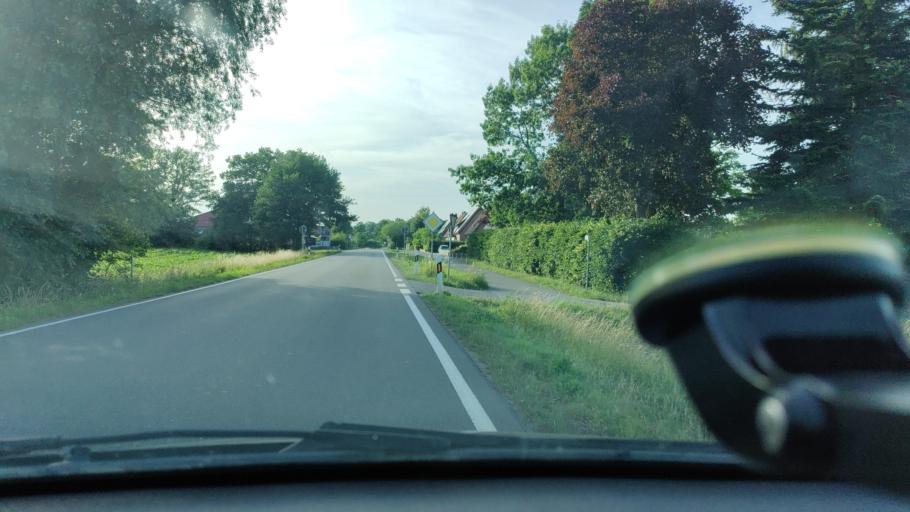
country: DE
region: North Rhine-Westphalia
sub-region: Regierungsbezirk Munster
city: Billerbeck
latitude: 51.9904
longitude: 7.2494
